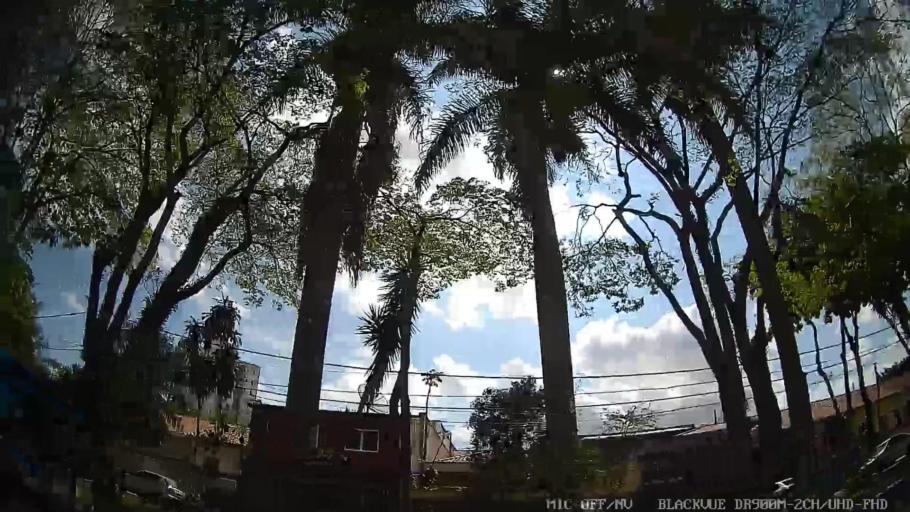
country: BR
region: Sao Paulo
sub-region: Guarulhos
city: Guarulhos
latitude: -23.4883
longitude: -46.4795
